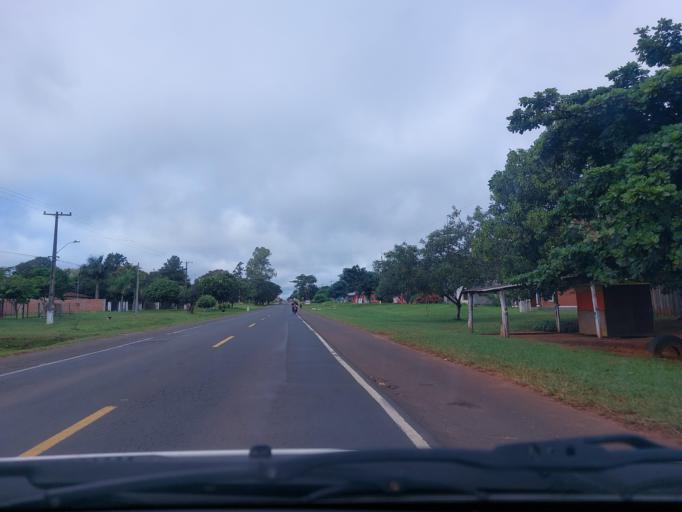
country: PY
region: San Pedro
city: Guayaybi
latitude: -24.5635
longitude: -56.4032
